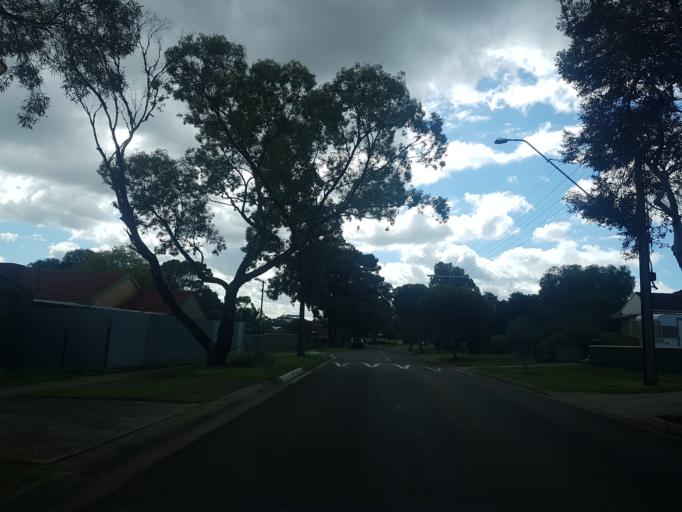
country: AU
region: South Australia
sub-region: Salisbury
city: Ingle Farm
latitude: -34.8158
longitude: 138.6464
